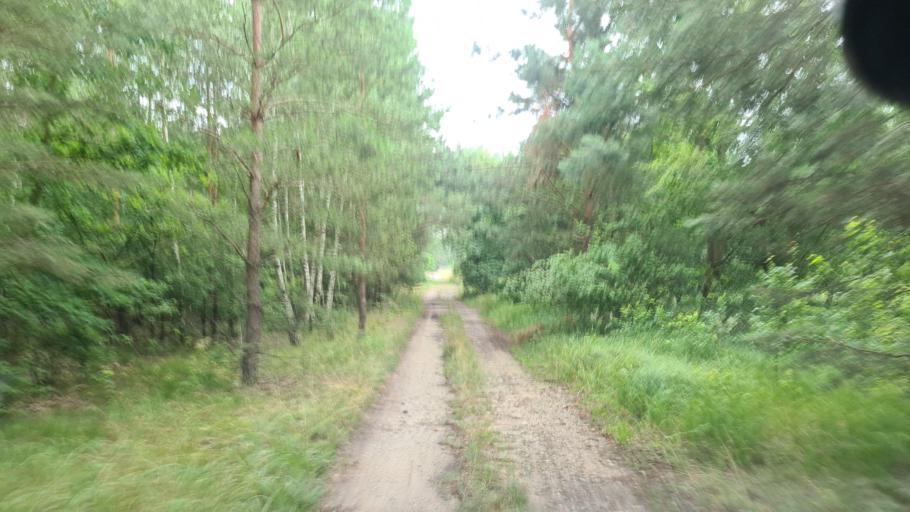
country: DE
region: Brandenburg
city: Sonnewalde
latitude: 51.7314
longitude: 13.6980
